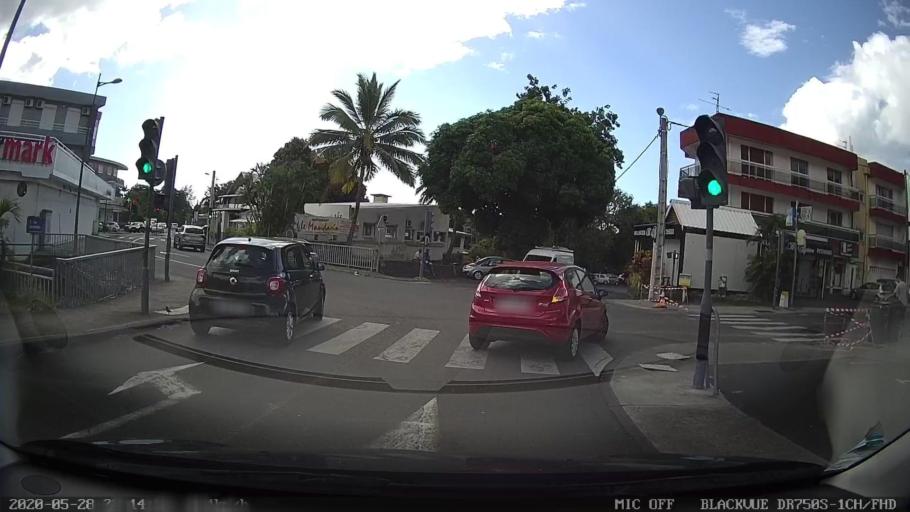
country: RE
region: Reunion
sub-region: Reunion
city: Saint-Denis
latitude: -20.8948
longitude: 55.4557
